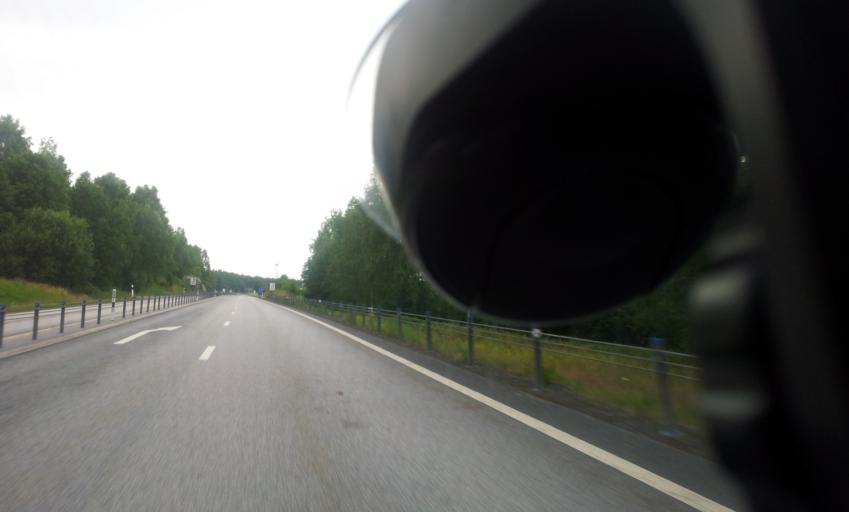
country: SE
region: OEstergoetland
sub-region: Valdemarsviks Kommun
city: Valdemarsvik
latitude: 58.1156
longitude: 16.5411
